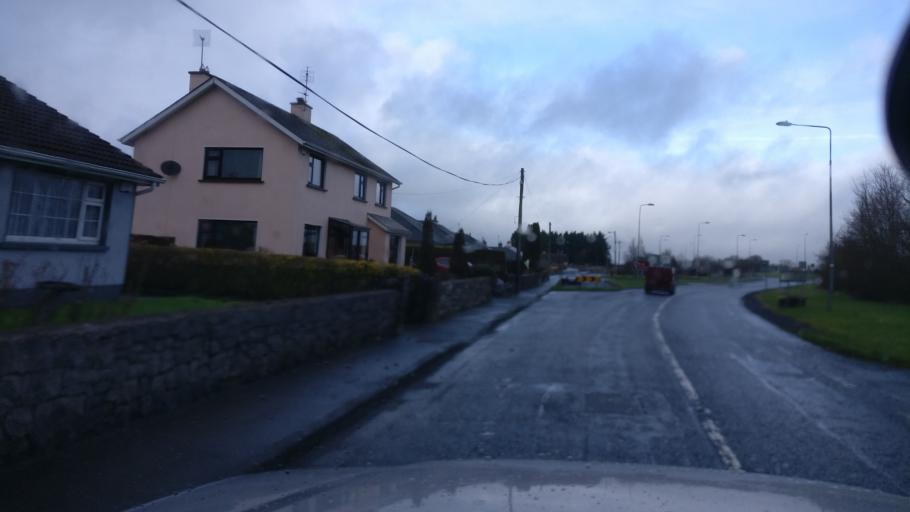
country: IE
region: Connaught
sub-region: County Galway
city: Loughrea
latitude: 53.2059
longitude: -8.5710
